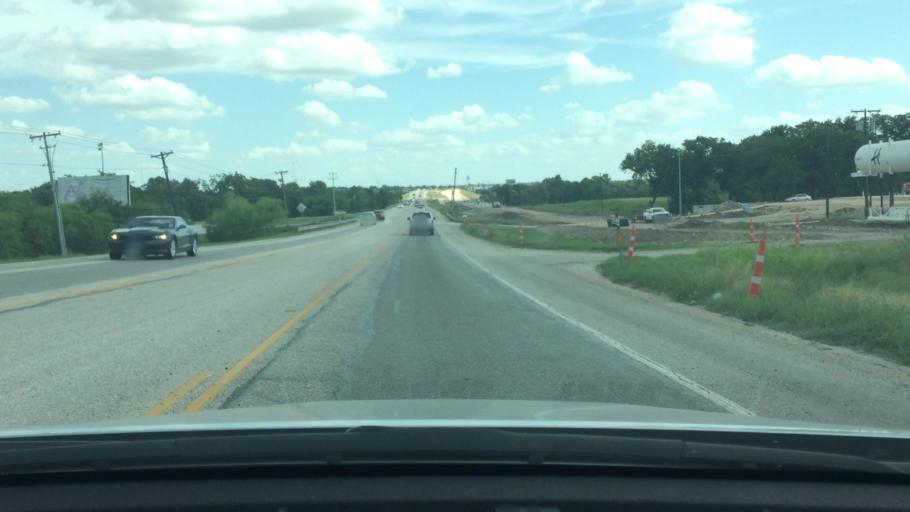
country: US
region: Texas
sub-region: Comal County
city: New Braunfels
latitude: 29.6921
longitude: -98.1552
